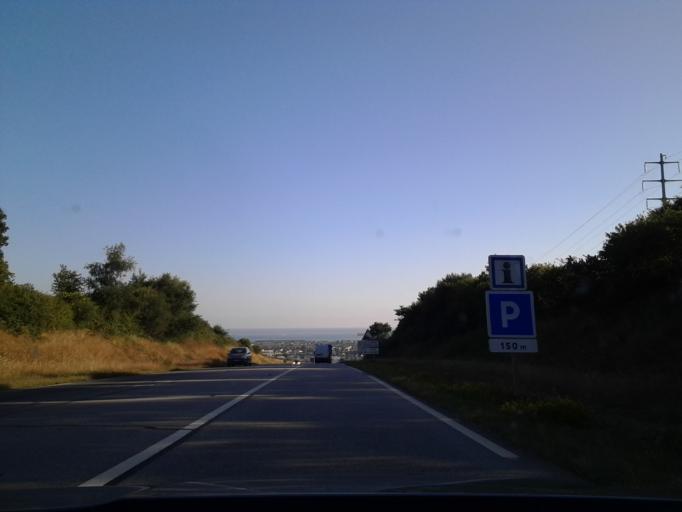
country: FR
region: Lower Normandy
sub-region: Departement de la Manche
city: La Glacerie
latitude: 49.6249
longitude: -1.5817
